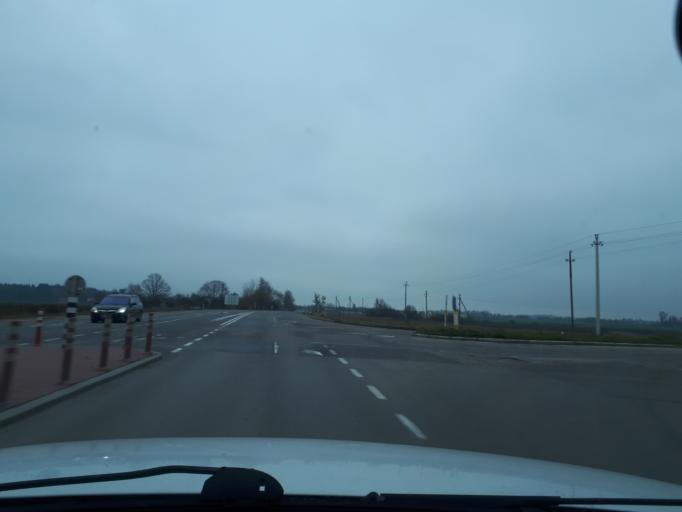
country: LT
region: Kauno apskritis
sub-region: Kauno rajonas
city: Akademija (Kaunas)
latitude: 54.8981
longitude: 23.7685
